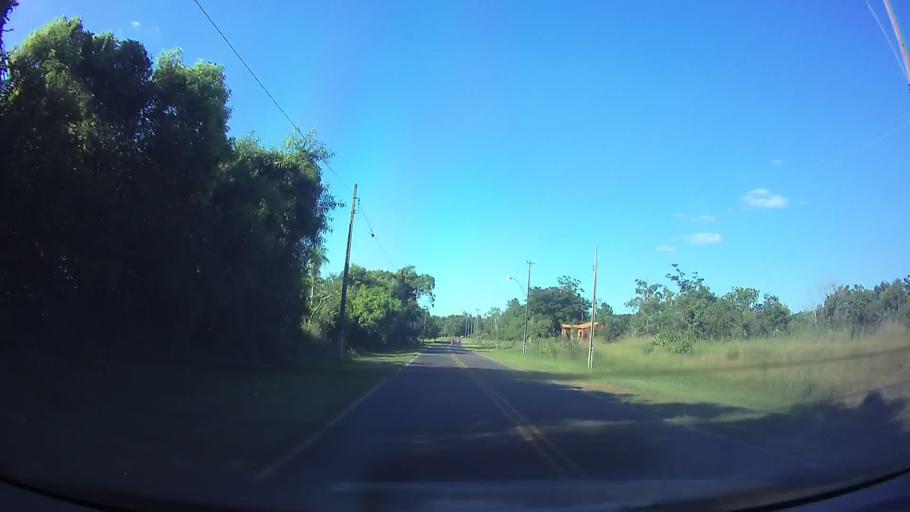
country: PY
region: Cordillera
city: Atyra
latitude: -25.3054
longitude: -57.1871
